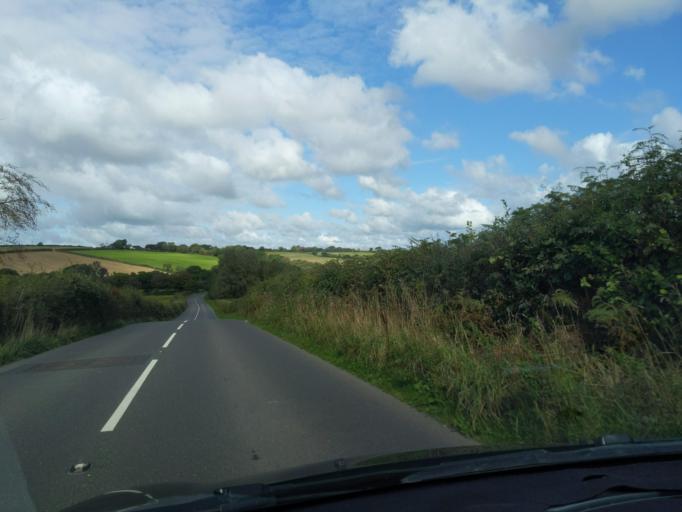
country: GB
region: England
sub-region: Devon
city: Holsworthy
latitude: 50.8663
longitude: -4.3233
